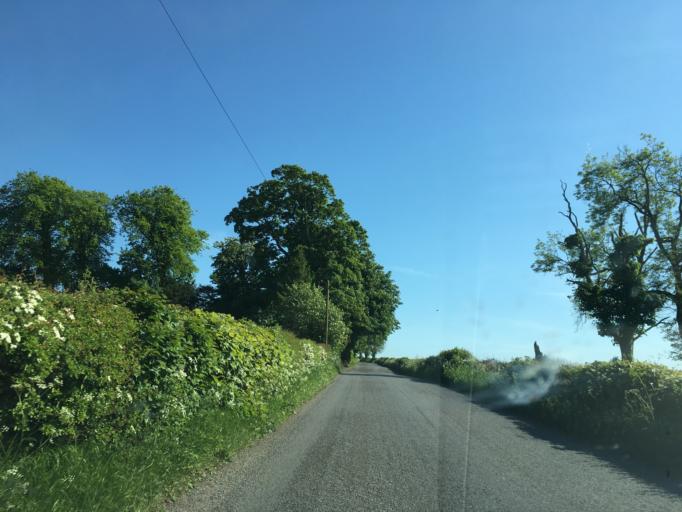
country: GB
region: Scotland
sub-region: Perth and Kinross
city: Methven
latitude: 56.3938
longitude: -3.5386
